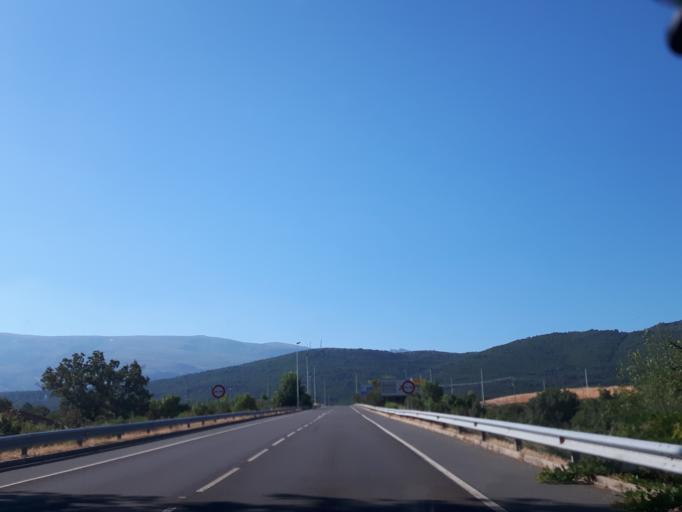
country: ES
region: Castille and Leon
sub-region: Provincia de Salamanca
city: Bejar
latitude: 40.3969
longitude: -5.7845
